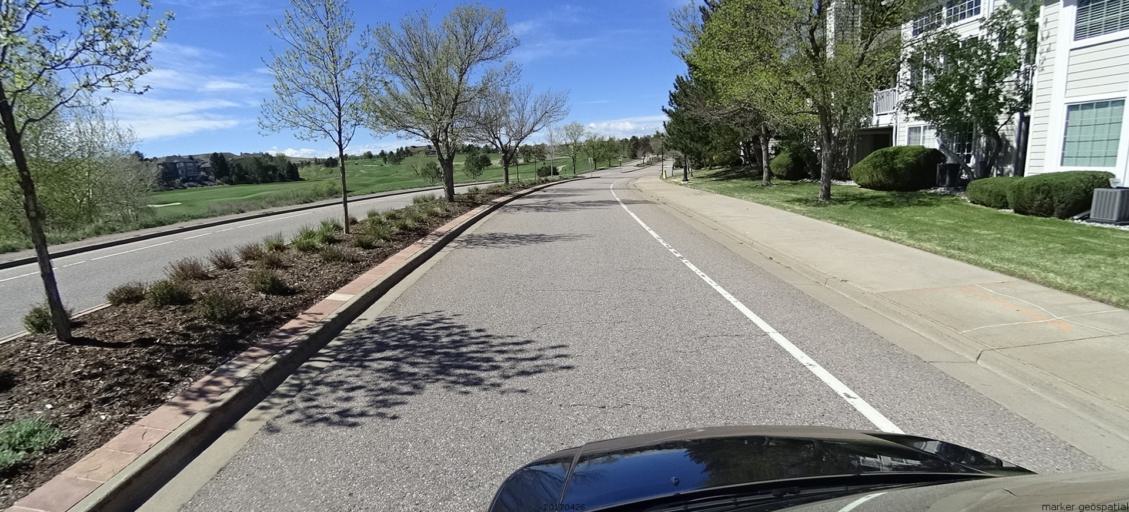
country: US
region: Colorado
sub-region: Adams County
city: Lone Tree
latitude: 39.5454
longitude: -104.8922
